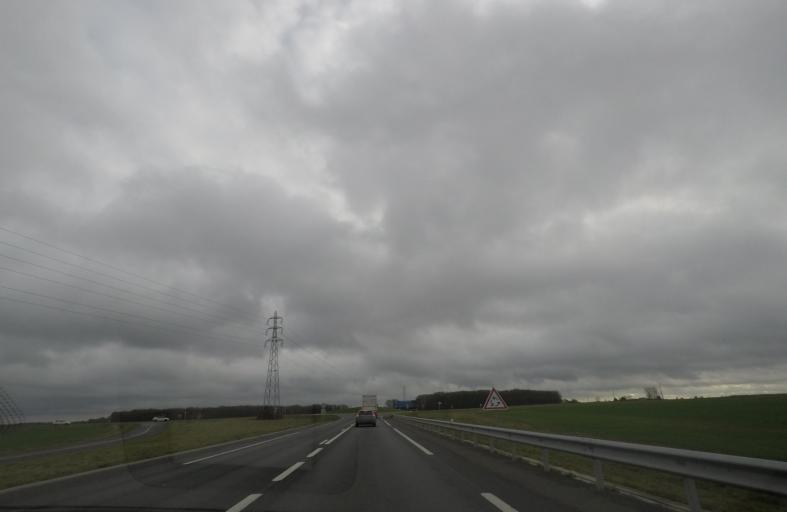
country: FR
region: Centre
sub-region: Departement du Loir-et-Cher
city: Vendome
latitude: 47.7676
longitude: 1.0710
